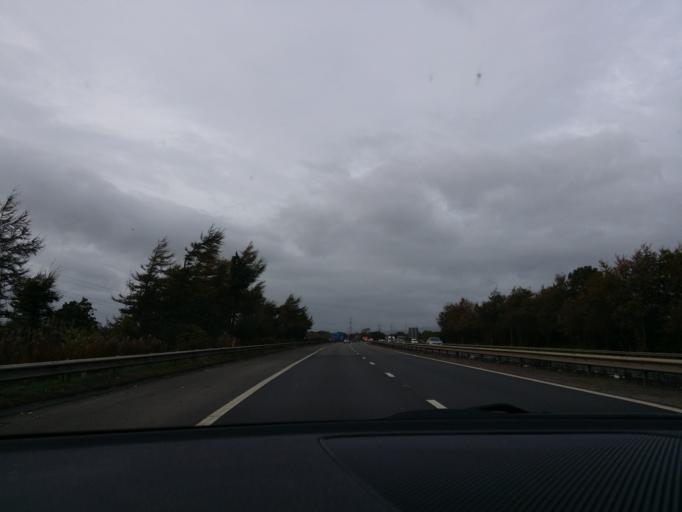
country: GB
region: Scotland
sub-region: Falkirk
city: Grangemouth
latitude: 56.0176
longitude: -3.7522
